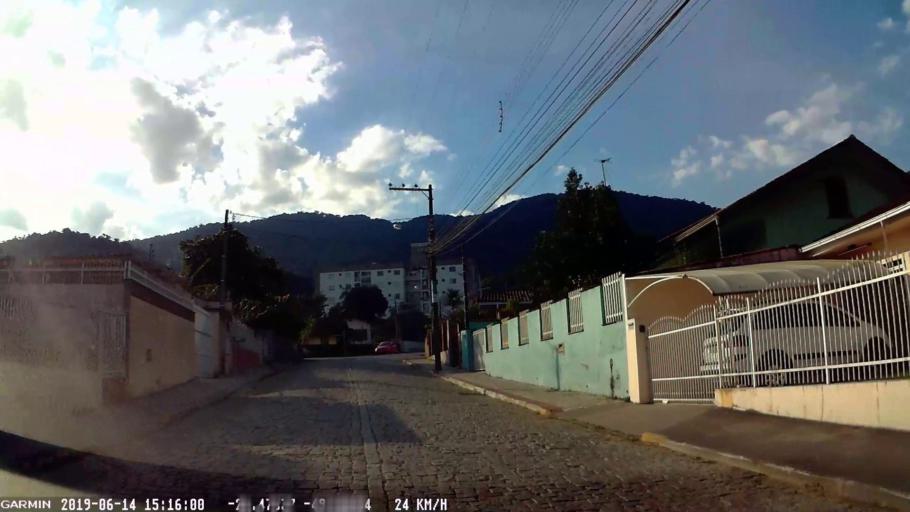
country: BR
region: Santa Catarina
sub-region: Jaragua Do Sul
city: Jaragua do Sul
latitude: -26.4733
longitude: -49.0829
